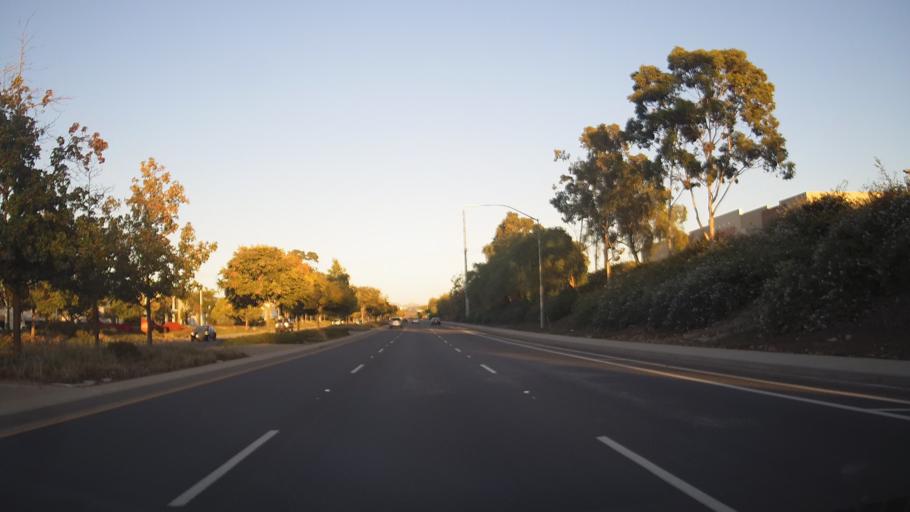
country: US
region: California
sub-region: San Diego County
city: Poway
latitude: 32.9382
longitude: -117.0339
